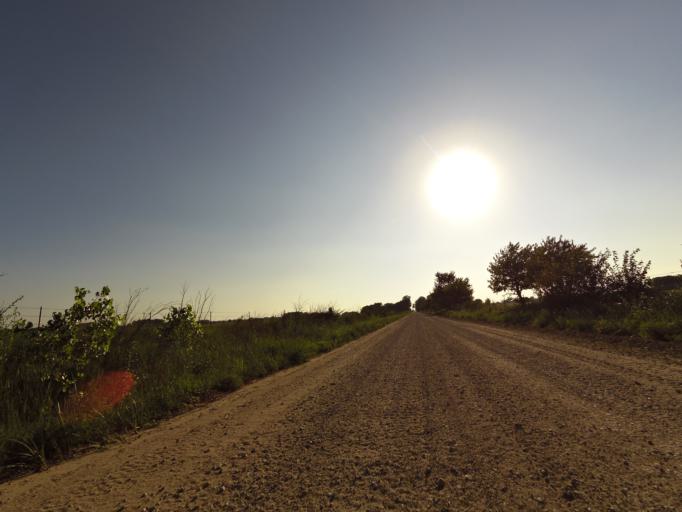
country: US
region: Kansas
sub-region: McPherson County
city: Inman
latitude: 38.1883
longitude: -97.8743
